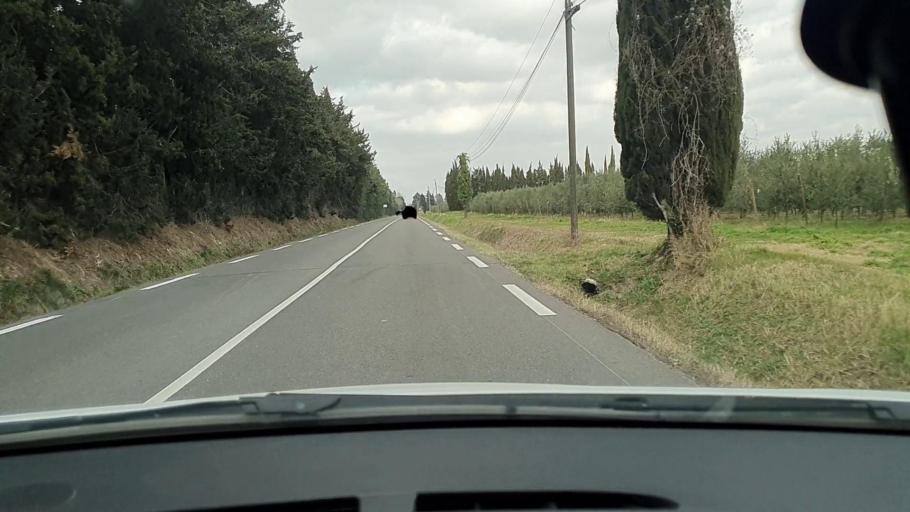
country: FR
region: Languedoc-Roussillon
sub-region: Departement du Gard
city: Meynes
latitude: 43.8892
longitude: 4.5749
